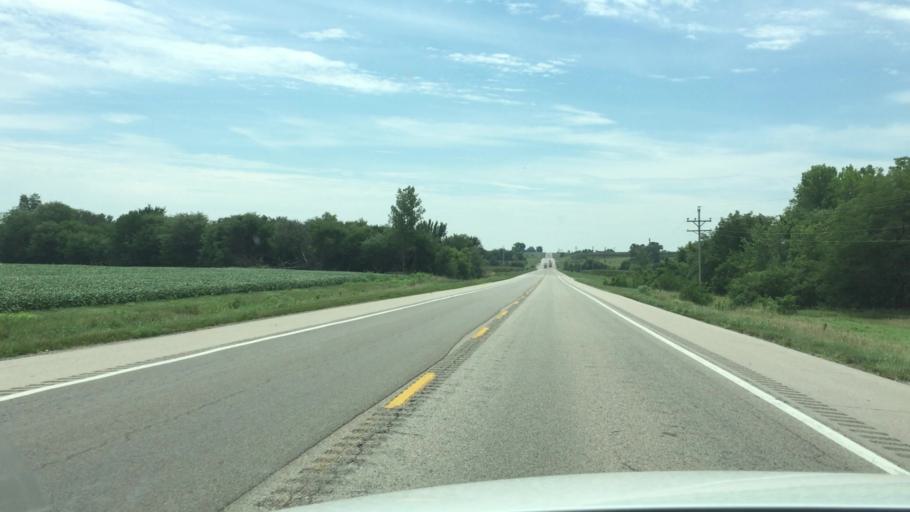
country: US
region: Kansas
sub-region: Nemaha County
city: Sabetha
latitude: 39.8061
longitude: -95.7294
